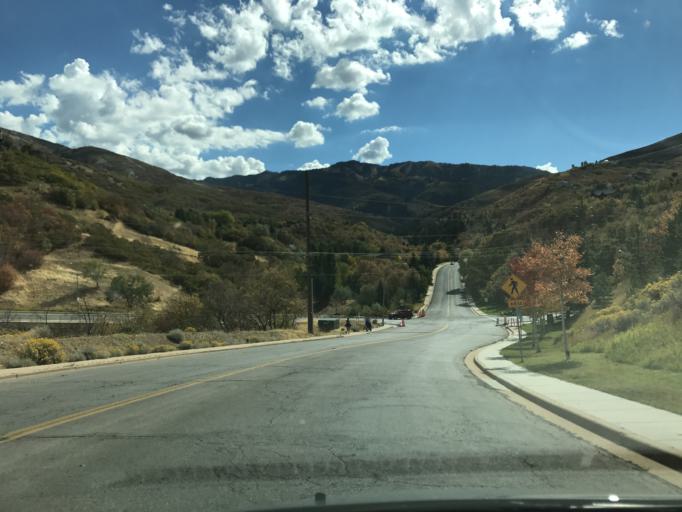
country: US
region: Utah
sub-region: Davis County
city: Bountiful
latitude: 40.8692
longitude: -111.8476
